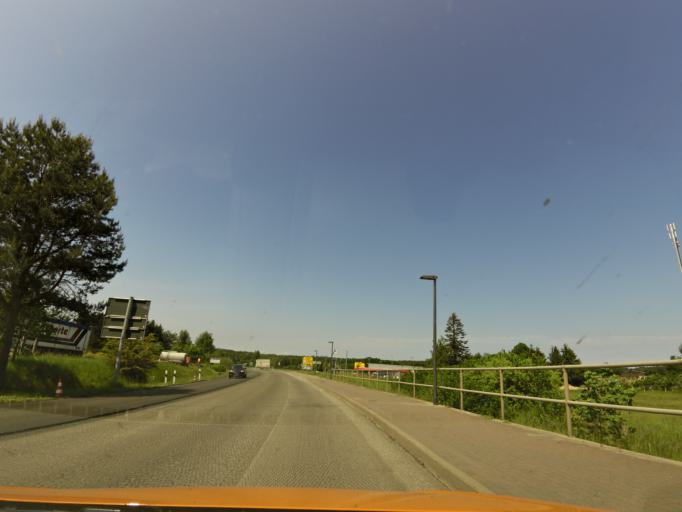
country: DE
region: Mecklenburg-Vorpommern
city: Selmsdorf
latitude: 53.8837
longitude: 10.8641
